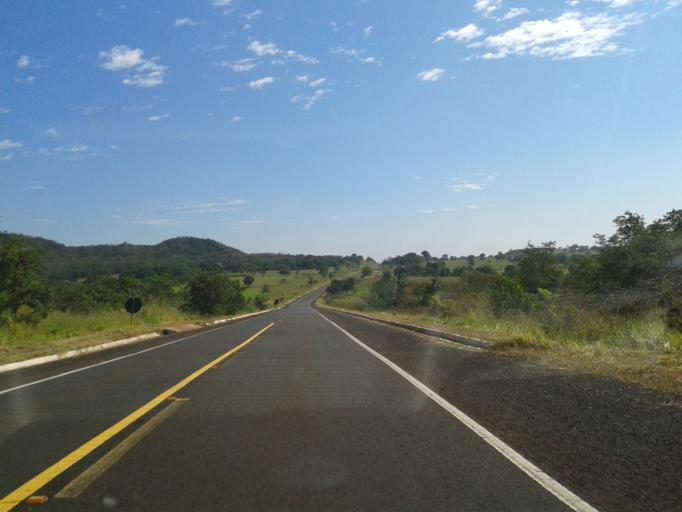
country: BR
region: Minas Gerais
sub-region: Santa Vitoria
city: Santa Vitoria
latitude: -19.2003
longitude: -50.0280
